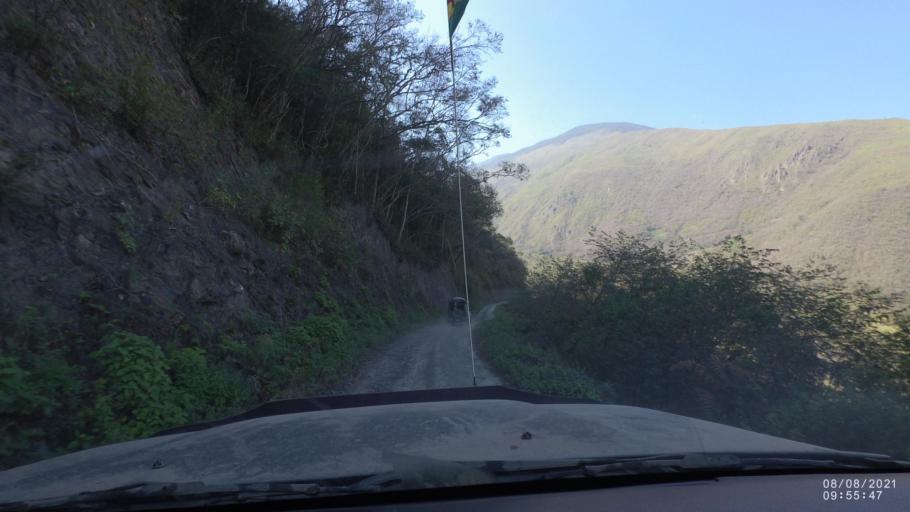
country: BO
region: La Paz
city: Quime
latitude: -16.6353
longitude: -66.7282
